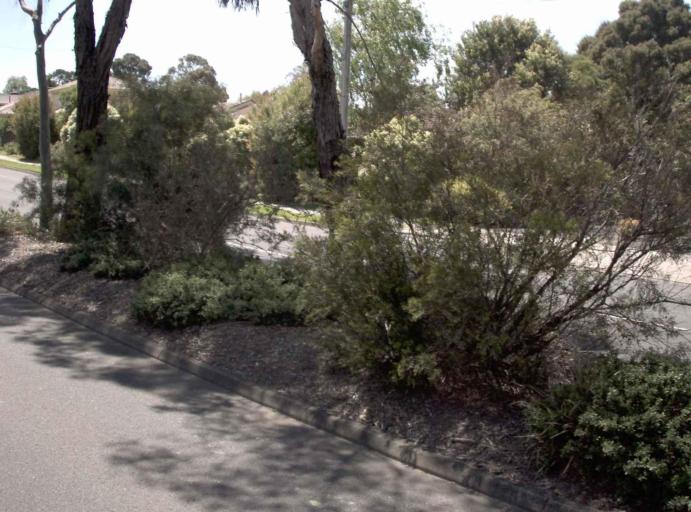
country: AU
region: Victoria
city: Burwood East
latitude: -37.8487
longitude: 145.1527
